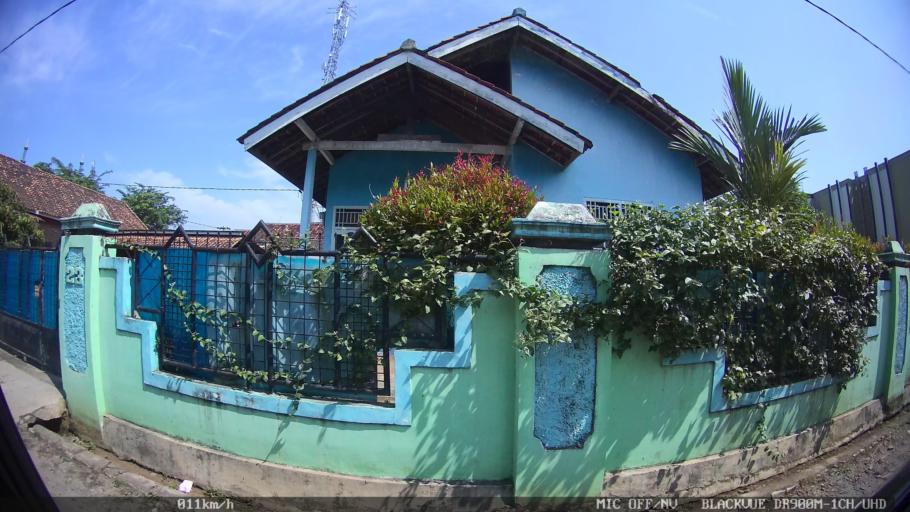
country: ID
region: Lampung
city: Kedaton
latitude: -5.3637
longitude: 105.2557
